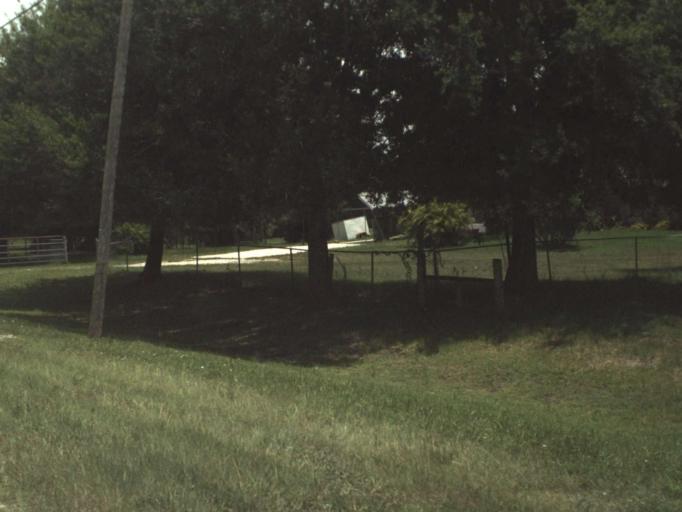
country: US
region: Florida
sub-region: Saint Lucie County
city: Fort Pierce South
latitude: 27.3744
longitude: -80.4357
